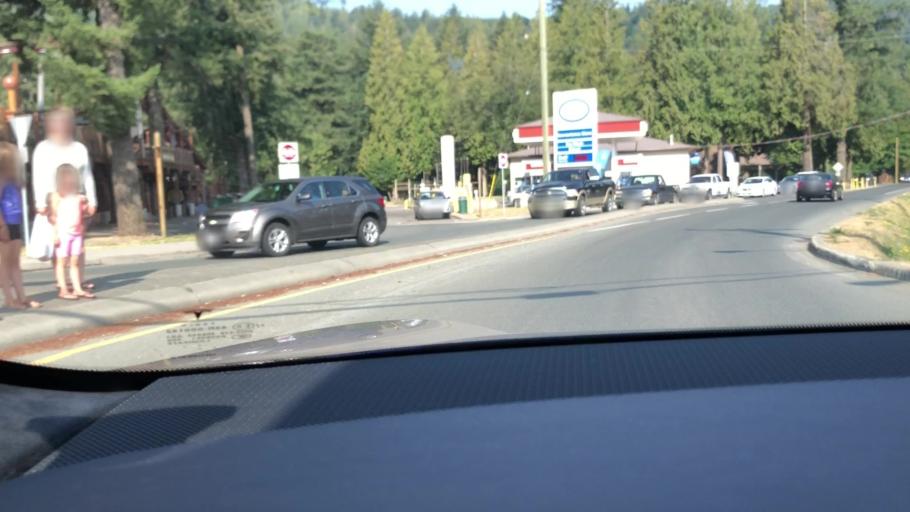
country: CA
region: British Columbia
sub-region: Fraser Valley Regional District
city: Chilliwack
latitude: 49.0755
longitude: -121.9764
